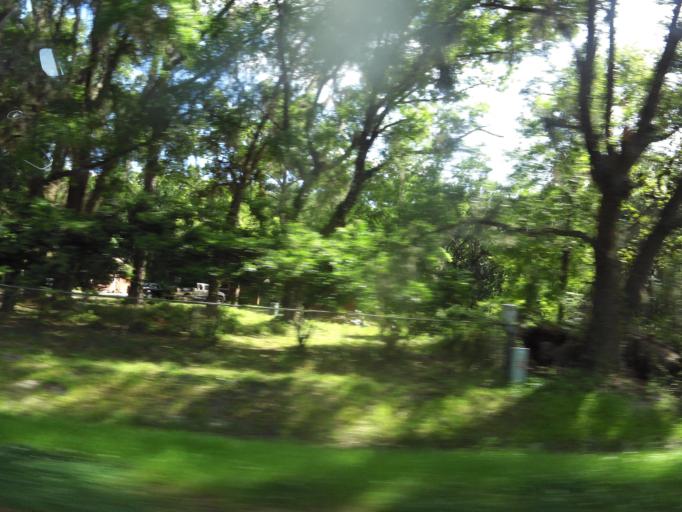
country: US
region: Florida
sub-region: Nassau County
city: Callahan
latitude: 30.5830
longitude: -81.8519
